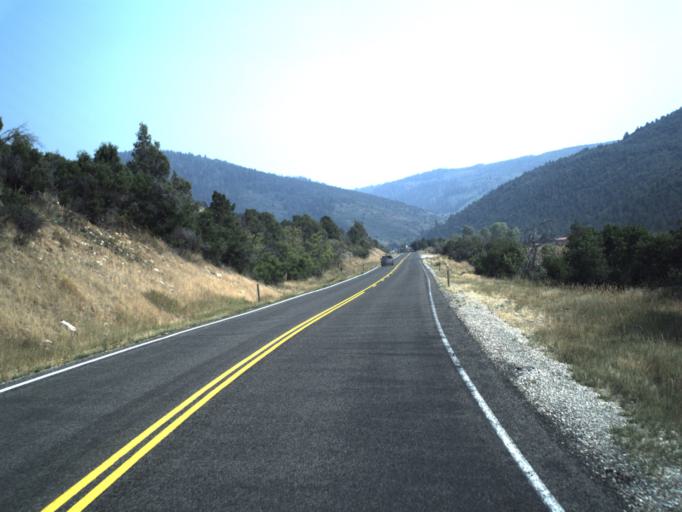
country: US
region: Utah
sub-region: Summit County
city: Francis
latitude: 40.6243
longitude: -111.2260
